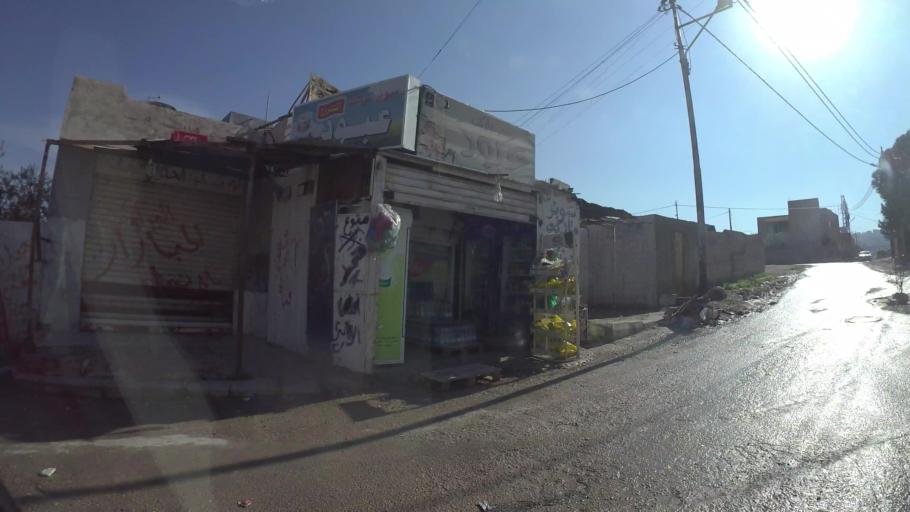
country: JO
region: Amman
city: Al Jubayhah
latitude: 32.0767
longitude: 35.8519
